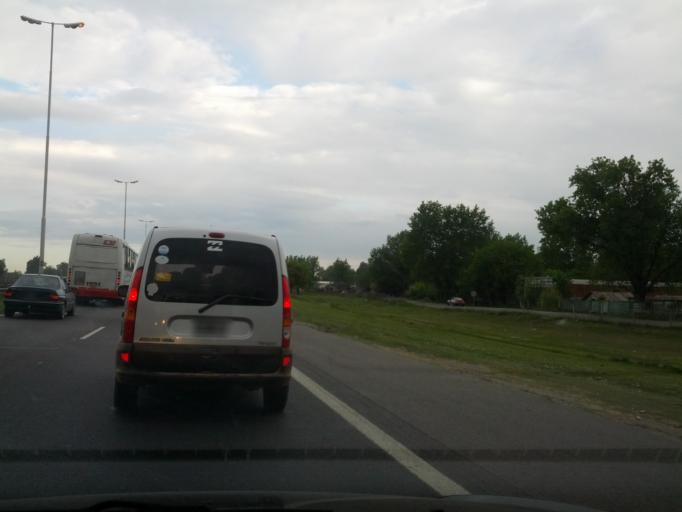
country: AR
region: Buenos Aires
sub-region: Partido de General Rodriguez
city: General Rodriguez
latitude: -34.6066
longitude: -58.8847
